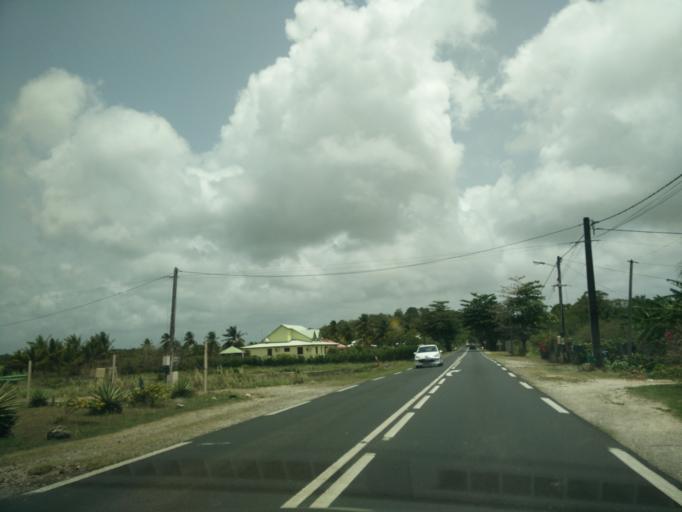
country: GP
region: Guadeloupe
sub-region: Guadeloupe
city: Petit-Canal
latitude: 16.3498
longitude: -61.4550
